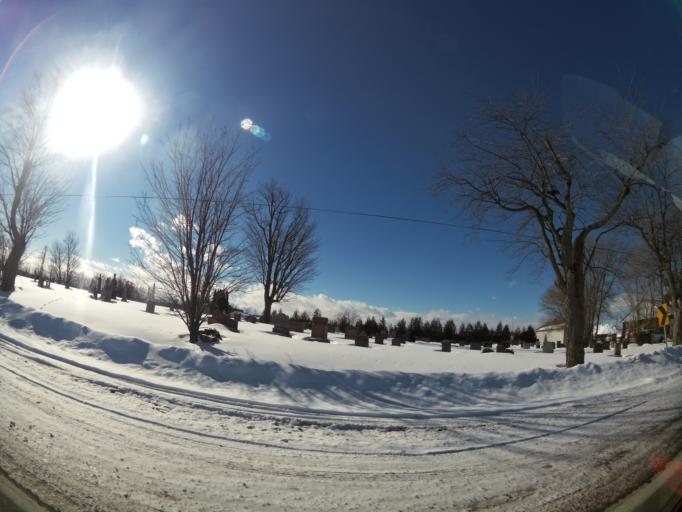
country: CA
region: Ontario
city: Ottawa
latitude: 45.3854
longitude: -75.5963
